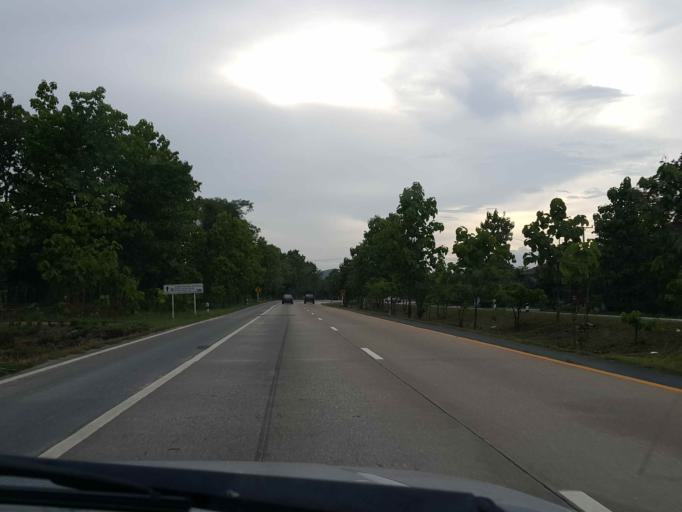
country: TH
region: Lamphun
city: Mae Tha
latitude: 18.4572
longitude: 99.1885
